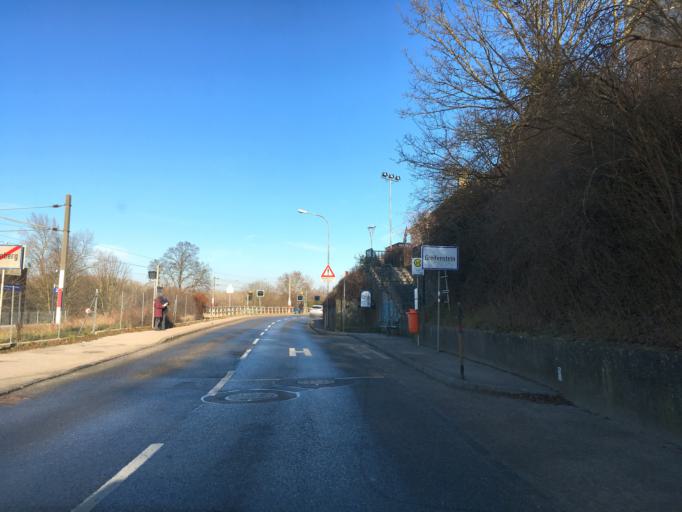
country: AT
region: Lower Austria
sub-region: Politischer Bezirk Tulln
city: Wordern
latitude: 48.3448
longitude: 16.2402
